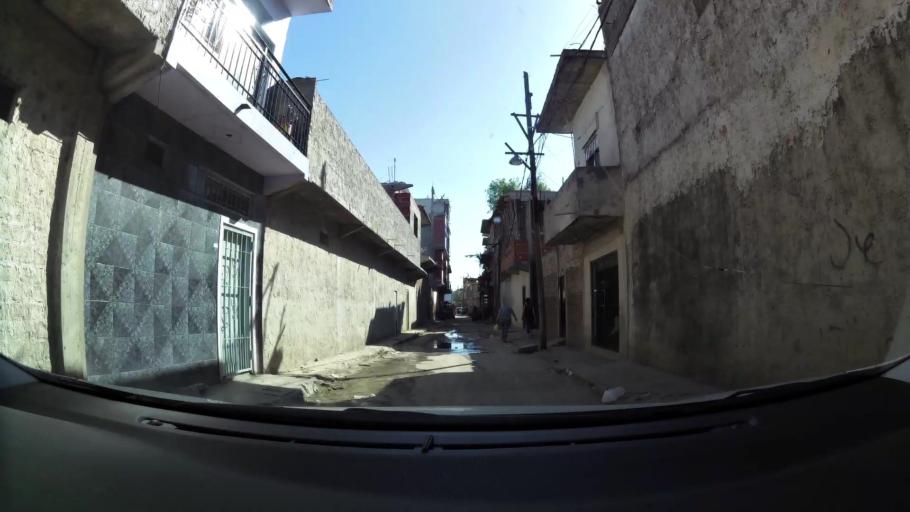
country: AR
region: Buenos Aires F.D.
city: Villa Lugano
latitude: -34.7091
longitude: -58.4850
